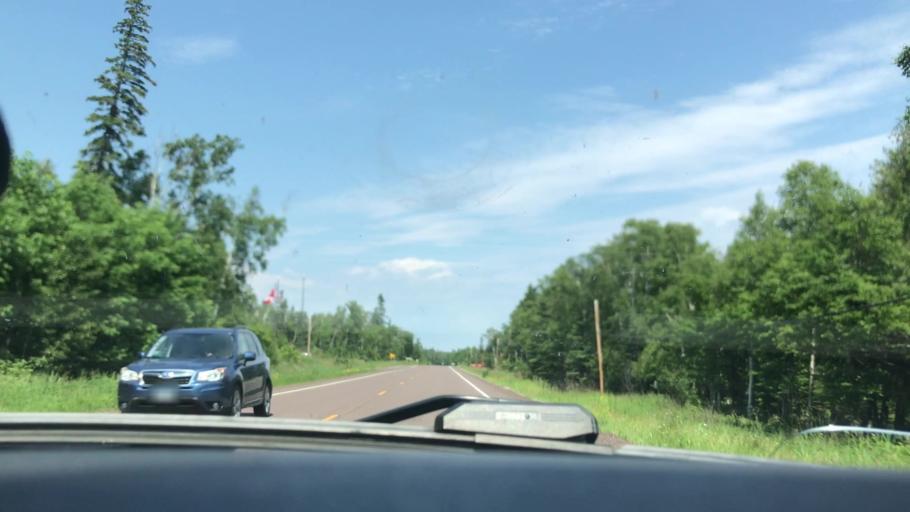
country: US
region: Minnesota
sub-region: Cook County
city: Grand Marais
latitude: 47.6360
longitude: -90.7143
